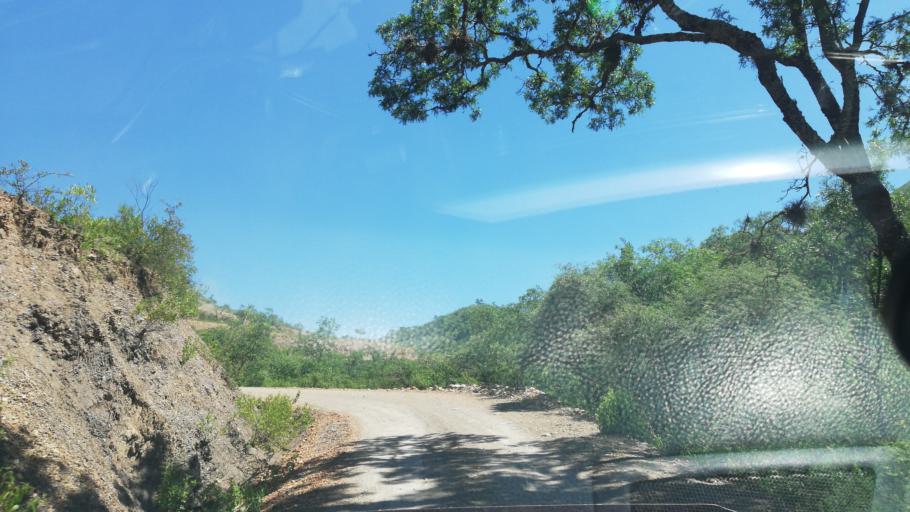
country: BO
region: Cochabamba
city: Mizque
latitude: -17.8806
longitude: -65.2877
